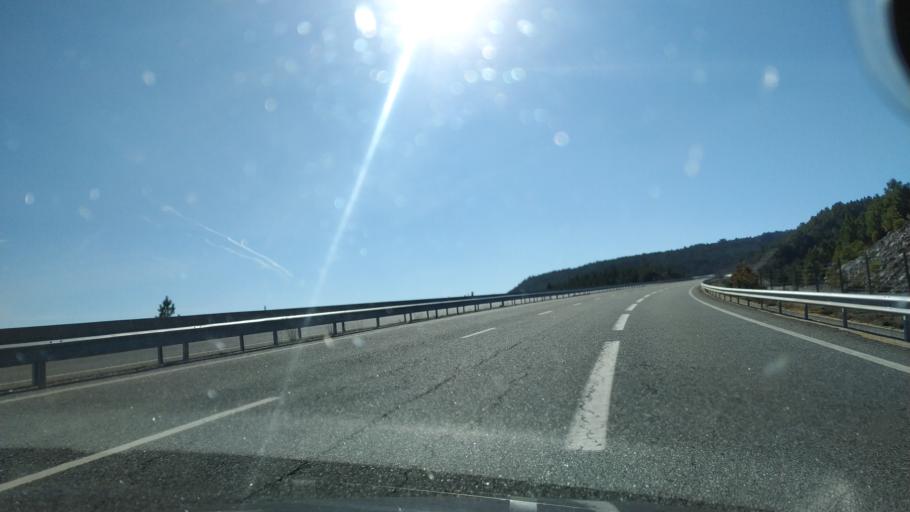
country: PT
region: Vila Real
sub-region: Vila Pouca de Aguiar
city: Vila Pouca de Aguiar
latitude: 41.5313
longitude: -7.6353
